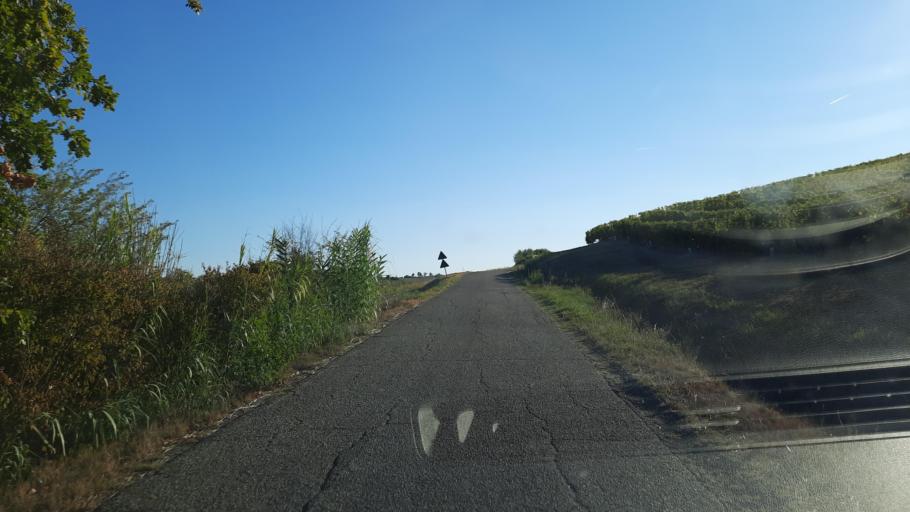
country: IT
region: Piedmont
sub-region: Provincia di Alessandria
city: Cuccaro Monferrato
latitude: 44.9970
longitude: 8.4414
